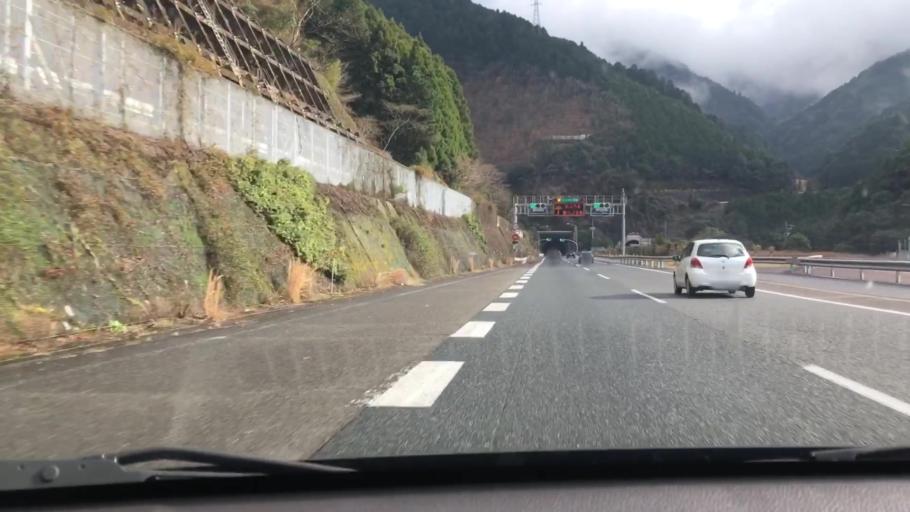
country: JP
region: Kumamoto
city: Yatsushiro
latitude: 32.3961
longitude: 130.7046
